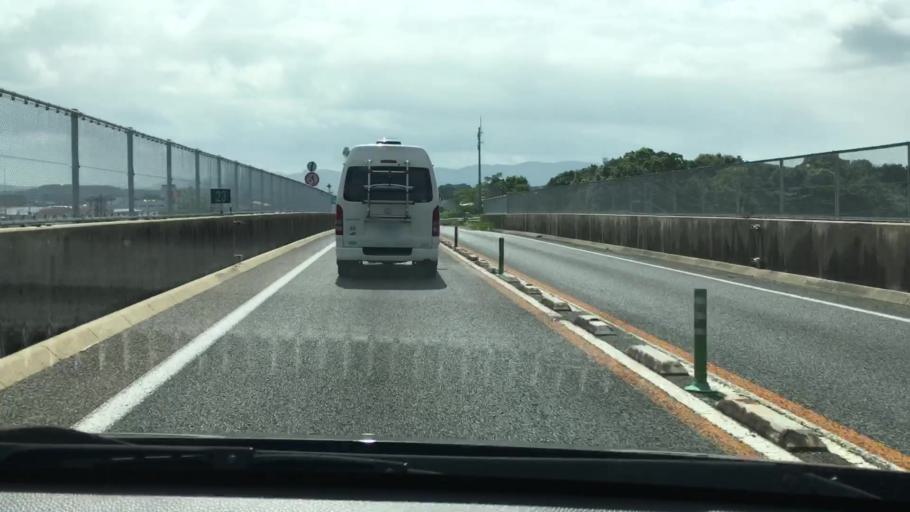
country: JP
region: Nagasaki
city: Sasebo
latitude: 33.1509
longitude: 129.7658
